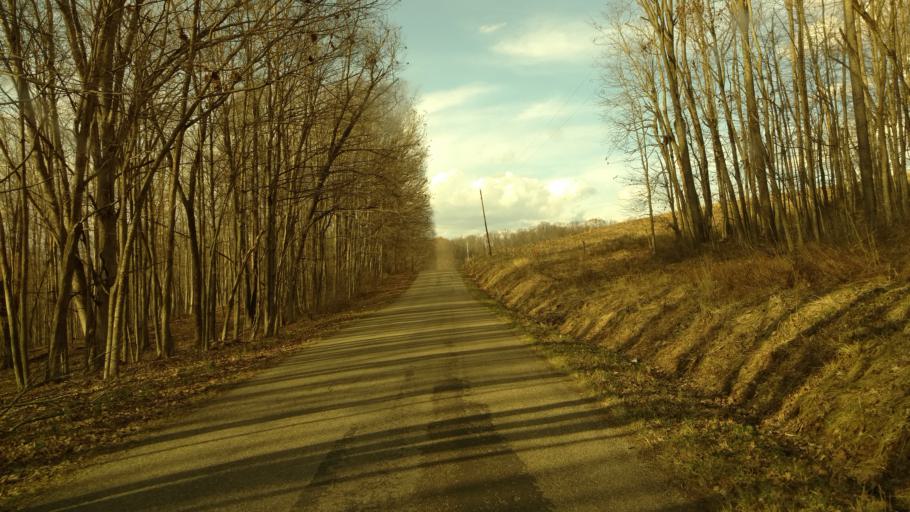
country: US
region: Ohio
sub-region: Sandusky County
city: Bellville
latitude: 40.5666
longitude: -82.4331
